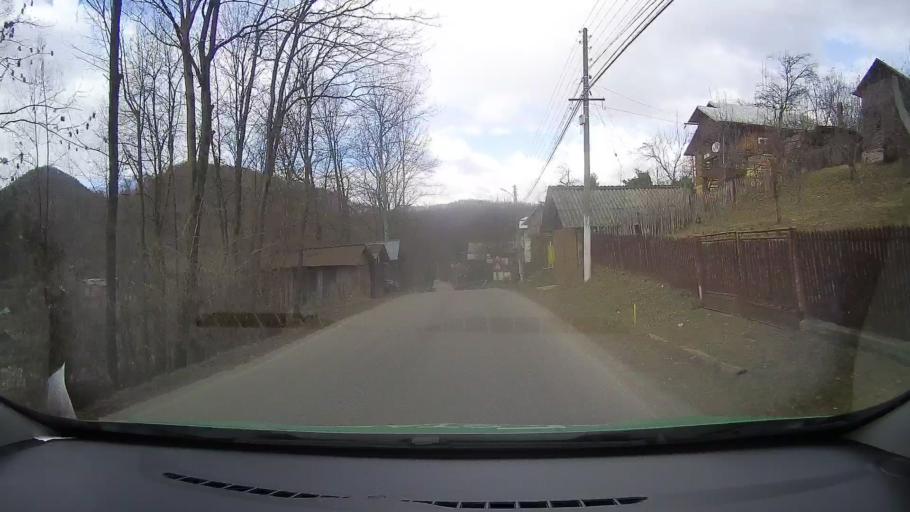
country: RO
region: Dambovita
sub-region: Comuna Visinesti
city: Visinesti
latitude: 45.1034
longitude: 25.5618
